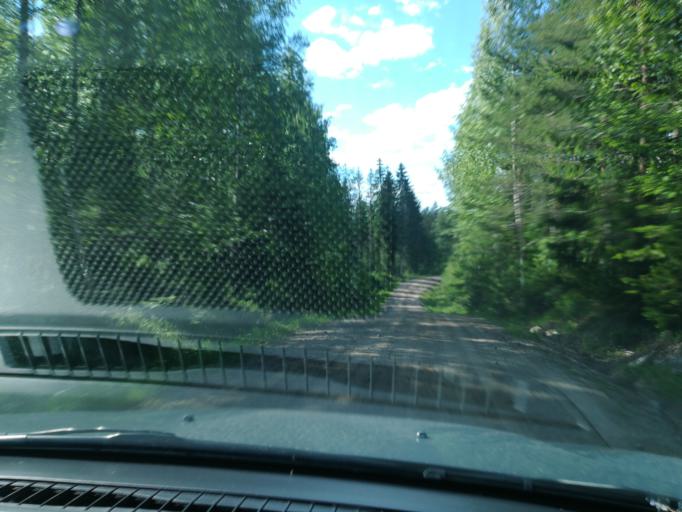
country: FI
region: Southern Savonia
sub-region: Mikkeli
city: Puumala
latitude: 61.6523
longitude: 28.1736
